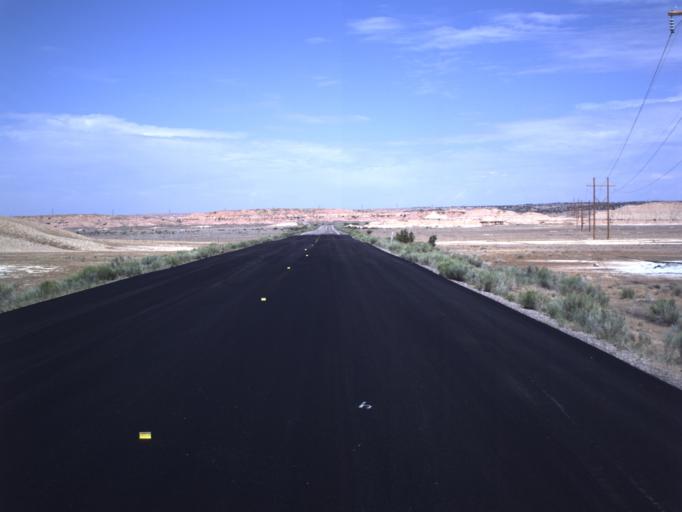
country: US
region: Utah
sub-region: Uintah County
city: Naples
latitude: 40.1166
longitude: -109.2465
